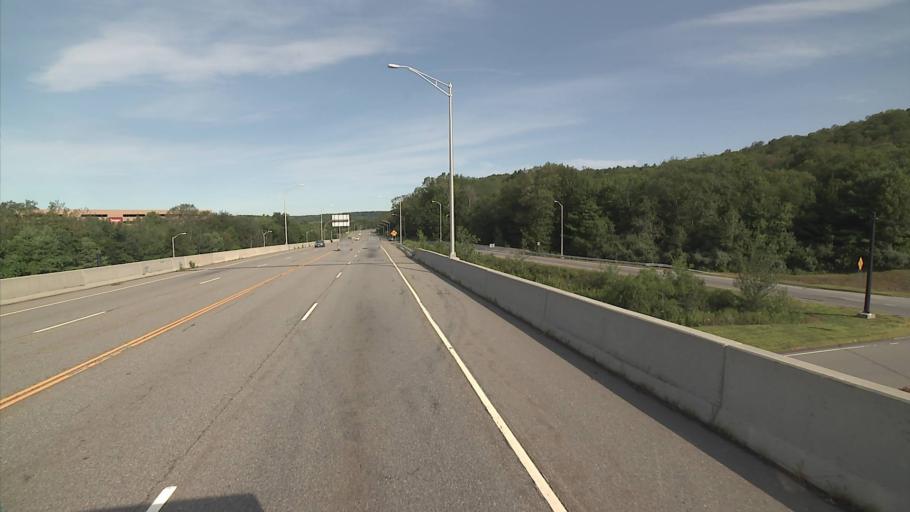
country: US
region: Connecticut
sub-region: New London County
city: Preston City
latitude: 41.4782
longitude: -71.9593
